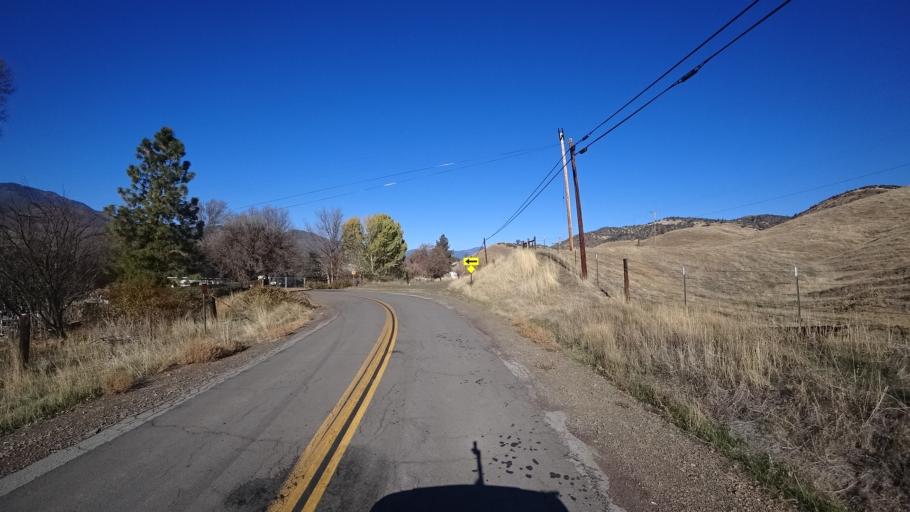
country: US
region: California
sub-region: Siskiyou County
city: Montague
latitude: 41.9088
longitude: -122.5516
